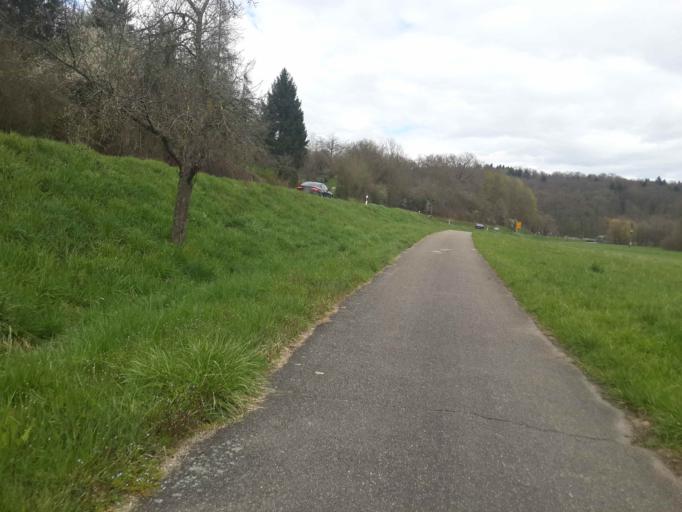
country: DE
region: Baden-Wuerttemberg
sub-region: Regierungsbezirk Stuttgart
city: Oedheim
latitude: 49.2743
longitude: 9.2231
